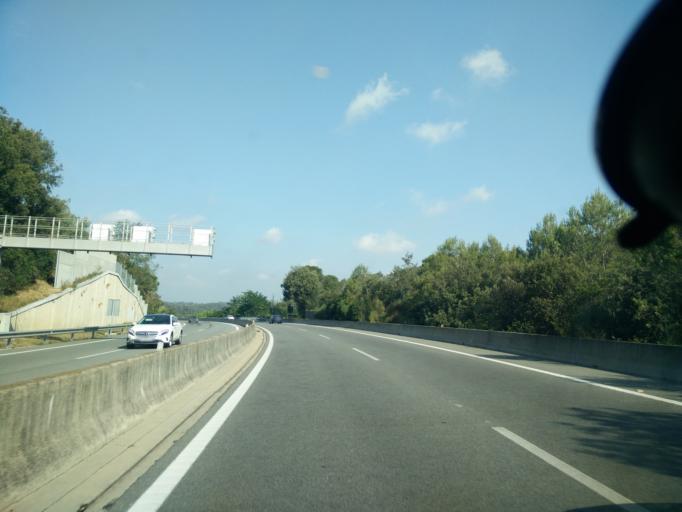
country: ES
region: Catalonia
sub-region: Provincia de Barcelona
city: Sant Cugat del Valles
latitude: 41.4270
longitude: 2.0908
